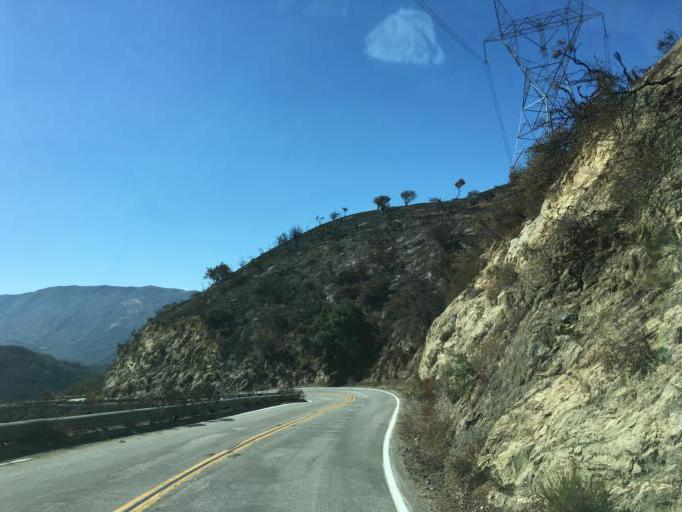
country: US
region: California
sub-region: Los Angeles County
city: San Fernando
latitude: 34.3373
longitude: -118.3398
